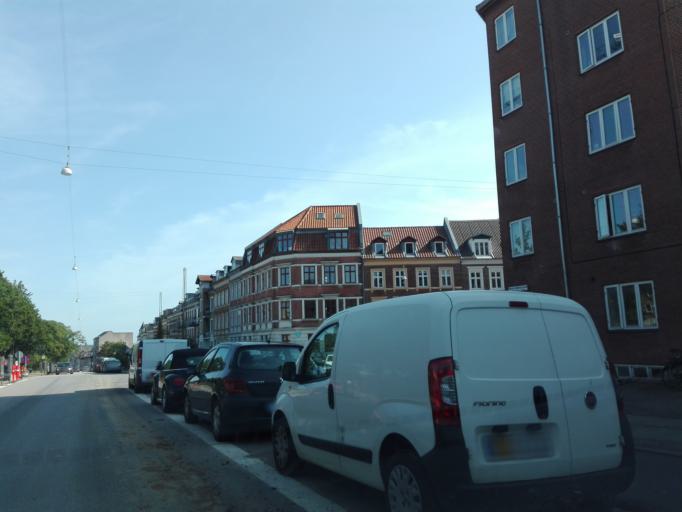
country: DK
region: Central Jutland
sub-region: Arhus Kommune
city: Arhus
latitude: 56.1649
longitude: 10.2024
